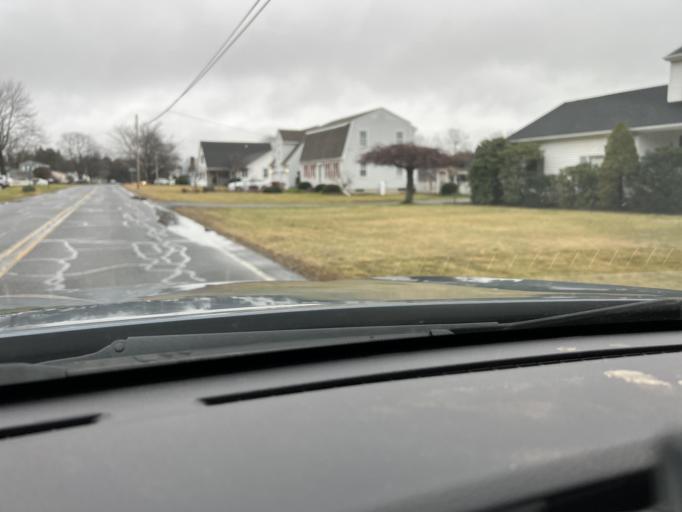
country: US
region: Massachusetts
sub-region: Hampden County
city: Southwick
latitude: 42.0399
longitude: -72.7049
